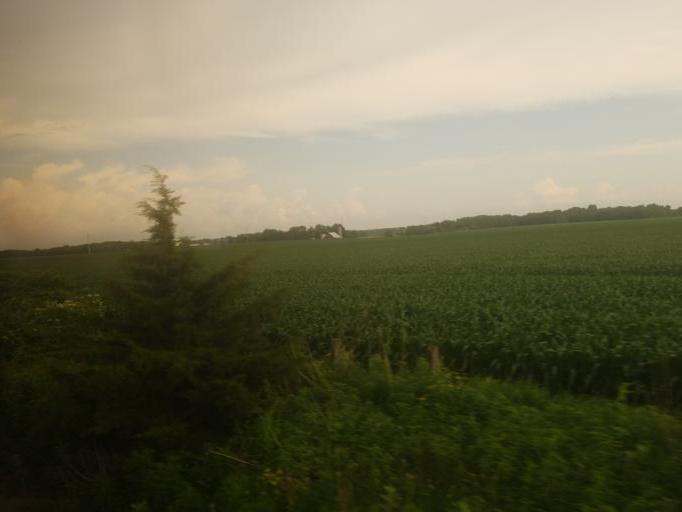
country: US
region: Illinois
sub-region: Bureau County
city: Princeton
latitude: 41.3934
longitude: -89.5006
